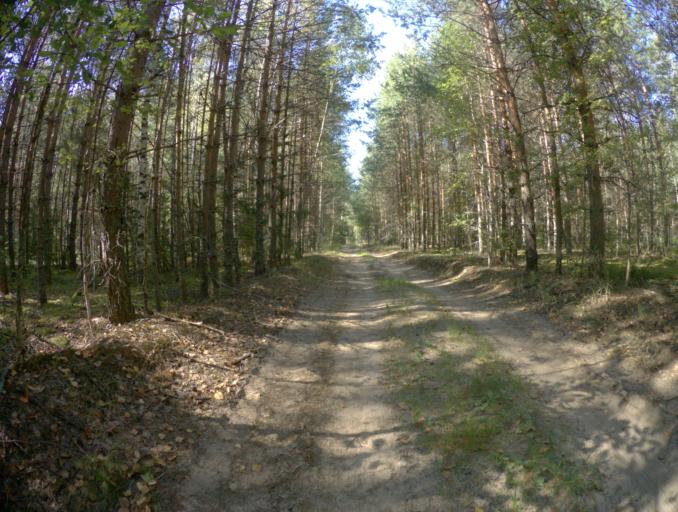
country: RU
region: Vladimir
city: Dobryatino
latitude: 55.7326
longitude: 41.4960
